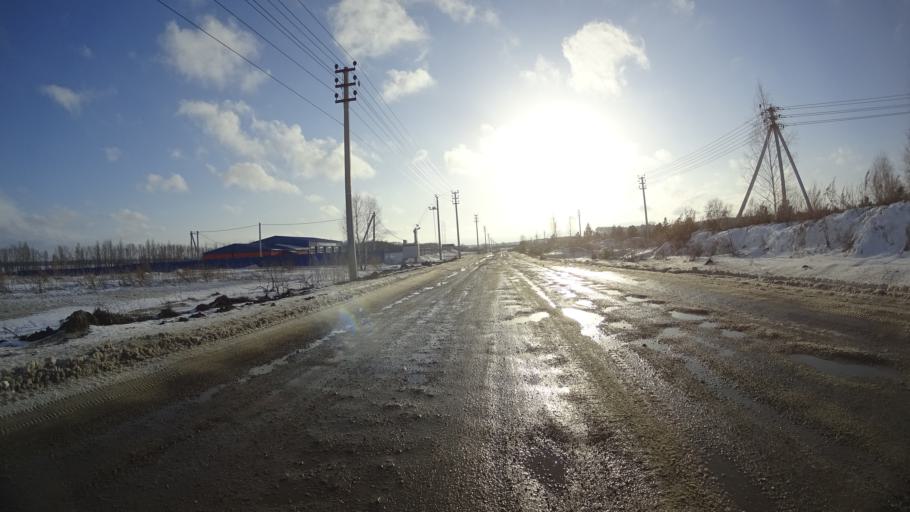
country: RU
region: Chelyabinsk
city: Sargazy
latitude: 55.1081
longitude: 61.2714
